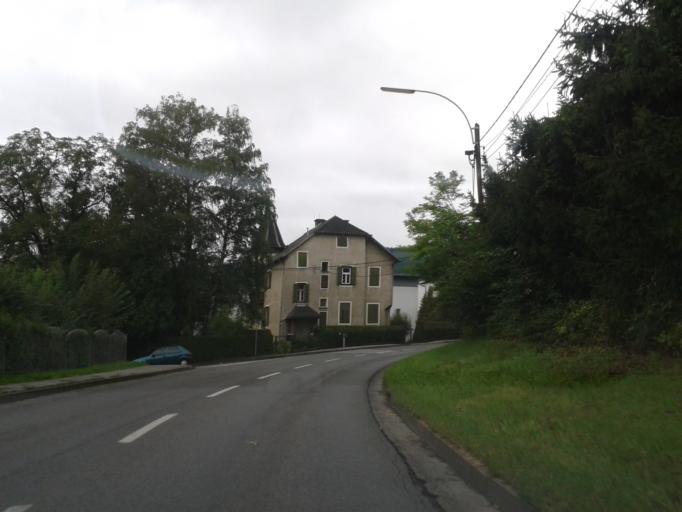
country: AT
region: Styria
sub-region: Graz Stadt
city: Goesting
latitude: 47.0805
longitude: 15.4017
